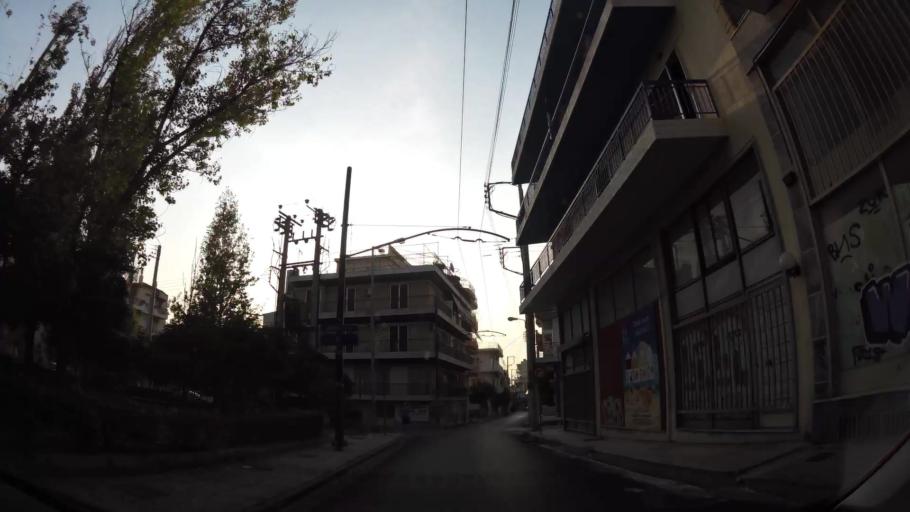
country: GR
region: Attica
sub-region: Nomarchia Athinas
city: Ilion
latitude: 38.0350
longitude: 23.6911
